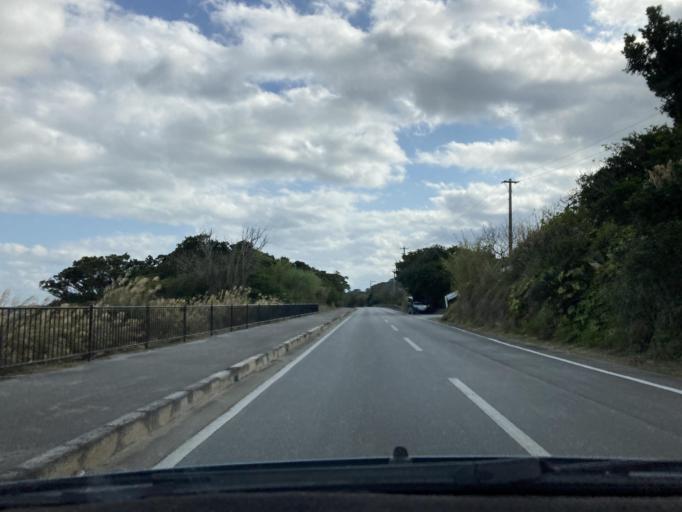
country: JP
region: Okinawa
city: Tomigusuku
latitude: 26.1802
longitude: 127.7604
